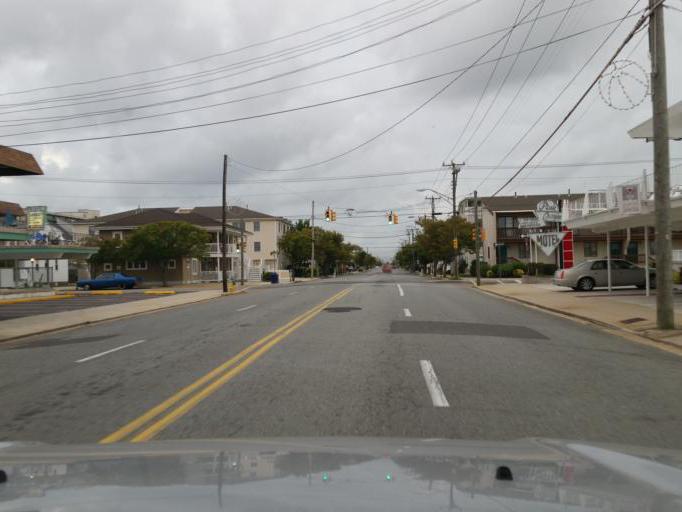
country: US
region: New Jersey
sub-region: Cape May County
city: Wildwood
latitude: 38.9813
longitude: -74.8217
